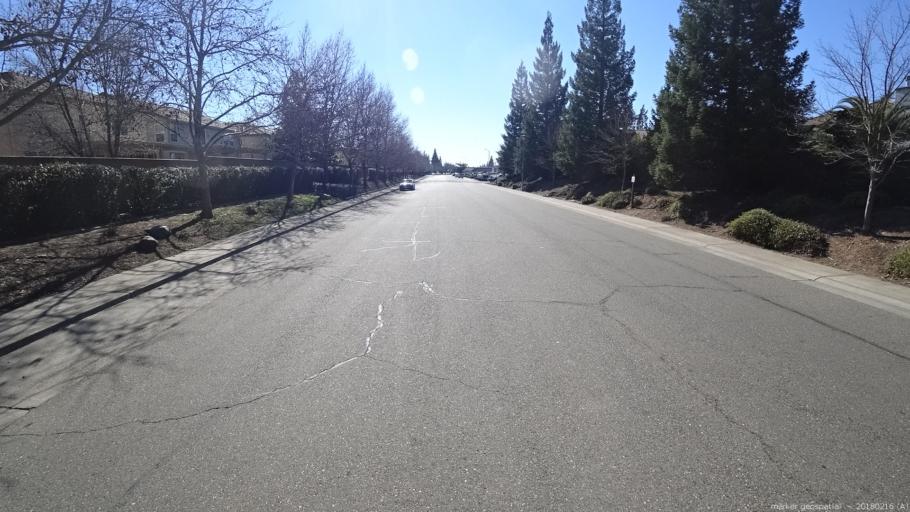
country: US
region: California
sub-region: Sacramento County
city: Gold River
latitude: 38.6188
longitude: -121.2518
